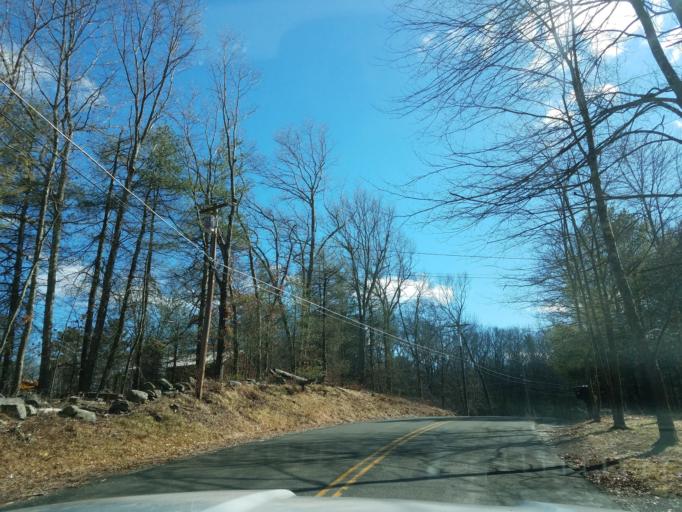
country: US
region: Connecticut
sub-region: Windham County
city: North Grosvenor Dale
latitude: 42.0100
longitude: -71.8704
